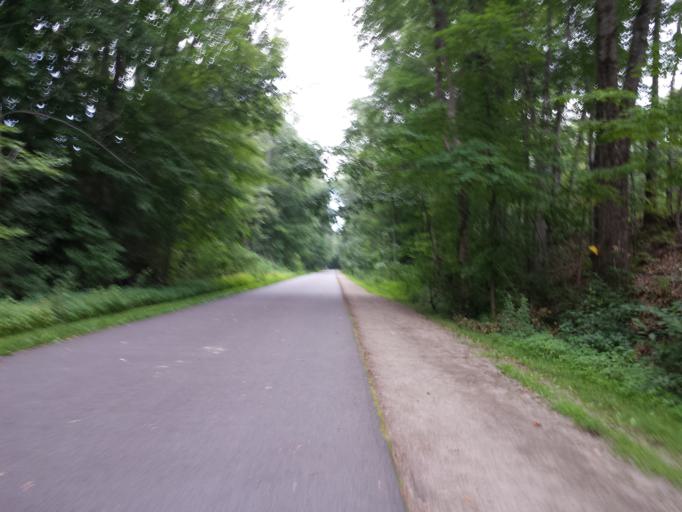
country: US
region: New York
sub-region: Dutchess County
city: Myers Corner
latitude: 41.6186
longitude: -73.8479
